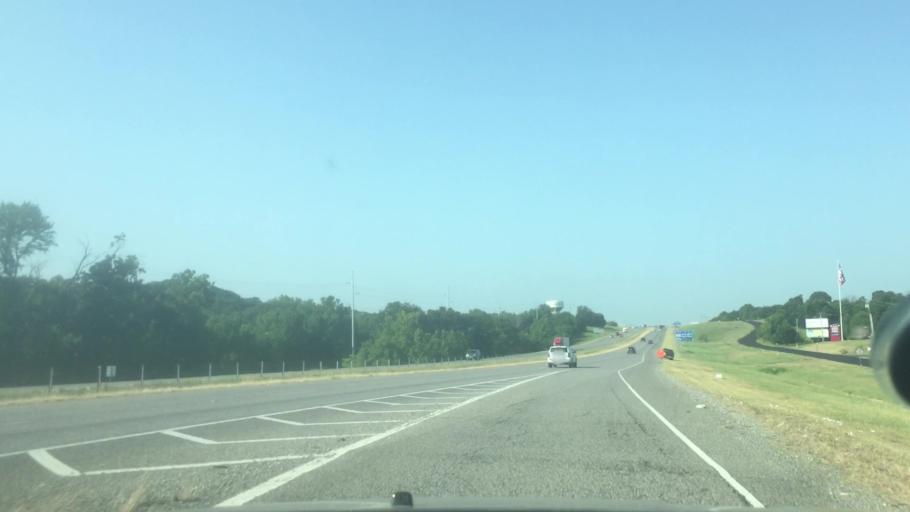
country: US
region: Oklahoma
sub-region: Bryan County
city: Durant
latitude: 34.0181
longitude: -96.3913
